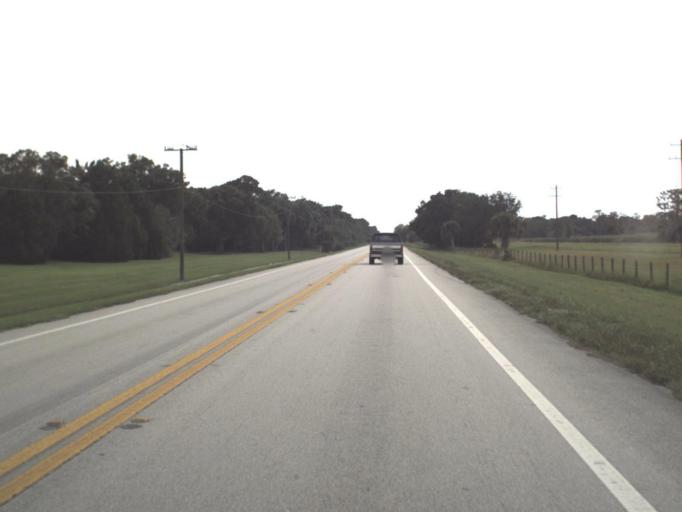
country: US
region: Florida
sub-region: Okeechobee County
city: Cypress Quarters
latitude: 27.3036
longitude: -80.8266
